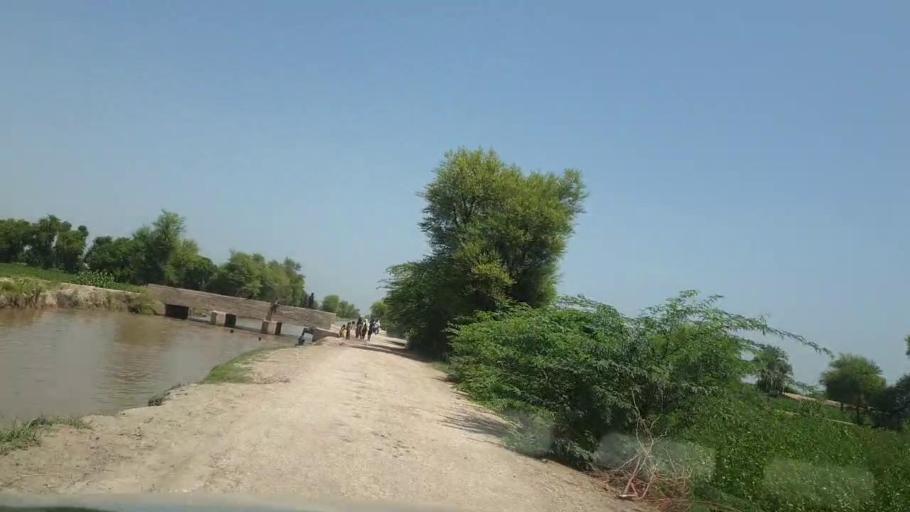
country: PK
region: Sindh
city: Pano Aqil
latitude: 27.6498
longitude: 69.1060
